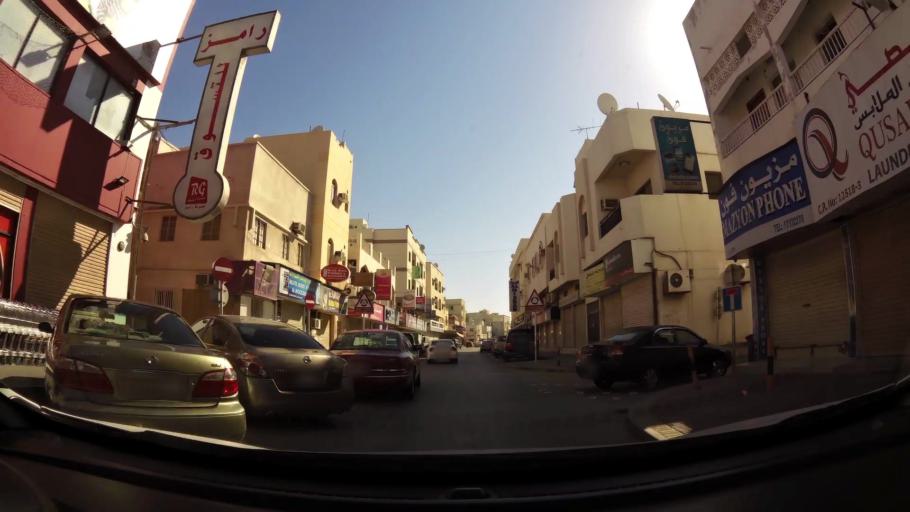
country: BH
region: Muharraq
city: Al Muharraq
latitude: 26.2619
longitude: 50.6135
